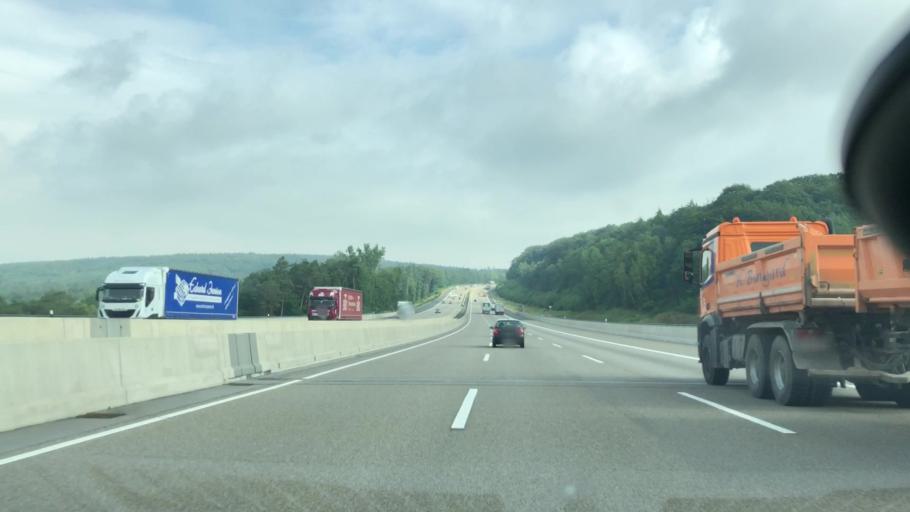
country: DE
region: Hesse
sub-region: Regierungsbezirk Kassel
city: Korle
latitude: 51.1417
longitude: 9.4757
